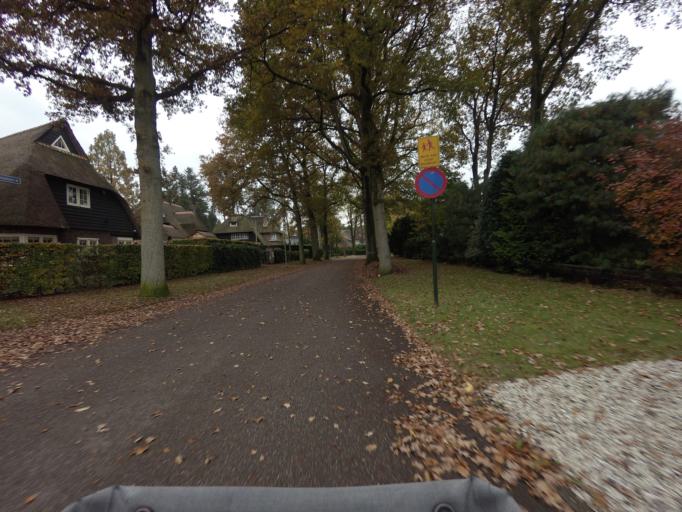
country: NL
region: North Holland
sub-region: Gemeente Hilversum
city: Hilversum
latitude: 52.2100
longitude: 5.1973
